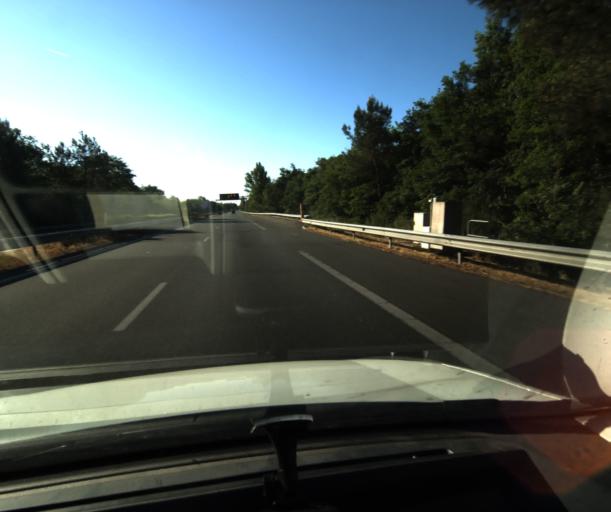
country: FR
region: Midi-Pyrenees
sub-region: Departement du Tarn-et-Garonne
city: Montech
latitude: 43.9623
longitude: 1.2772
